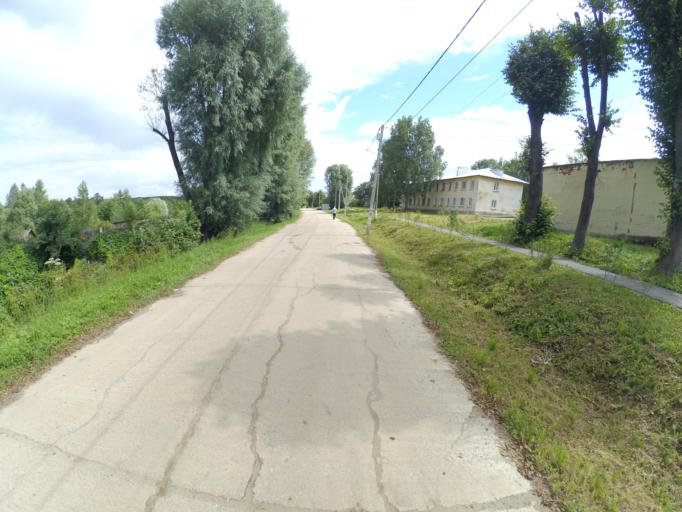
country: RU
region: Moskovskaya
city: Fosforitnyy
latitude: 55.3268
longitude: 38.8982
